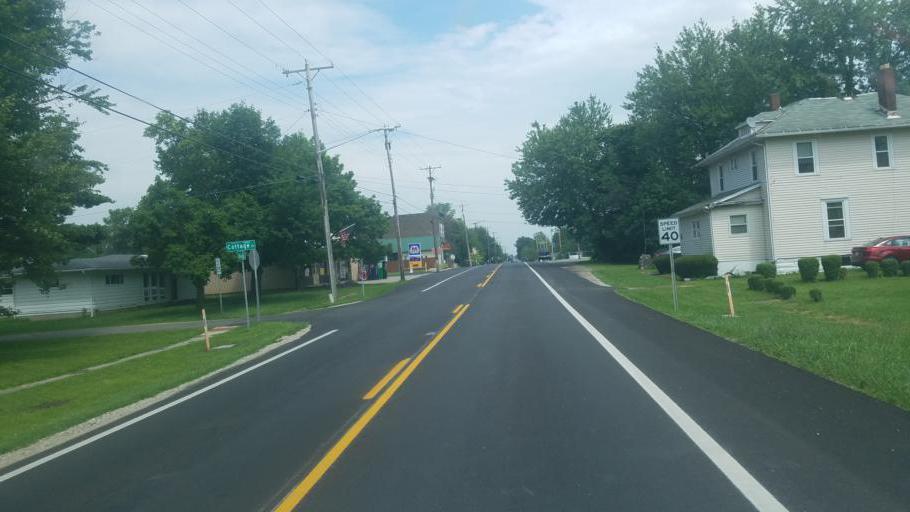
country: US
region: Ohio
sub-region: Union County
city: Marysville
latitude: 40.3406
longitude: -83.4164
